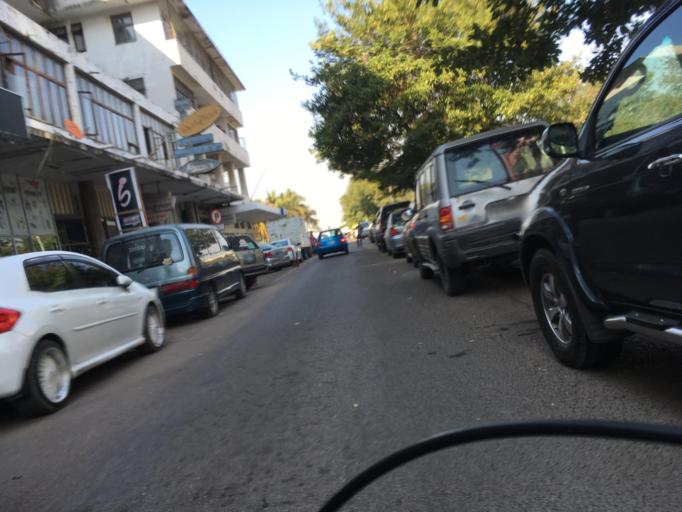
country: MZ
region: Maputo City
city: Maputo
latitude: -25.9737
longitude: 32.5706
